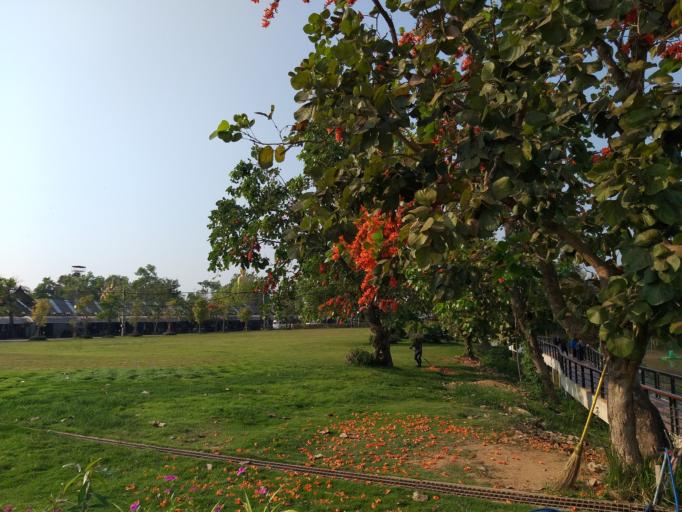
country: TH
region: Changwat Udon Thani
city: Ban Dung
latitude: 17.7426
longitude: 103.3602
